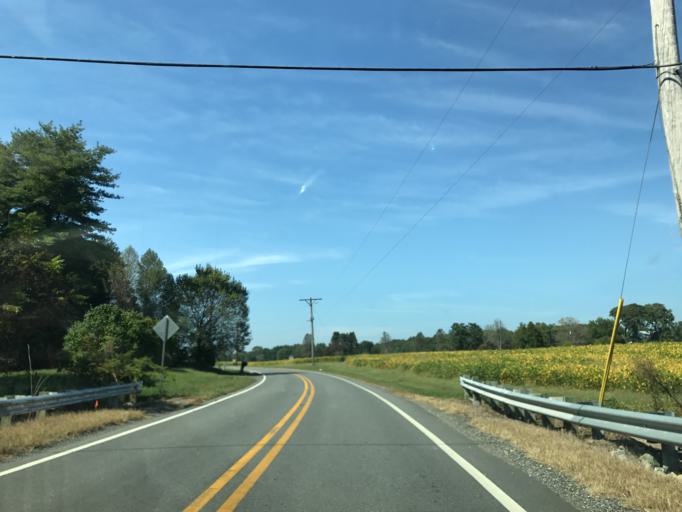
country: US
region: Delaware
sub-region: New Castle County
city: Townsend
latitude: 39.3006
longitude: -75.7502
